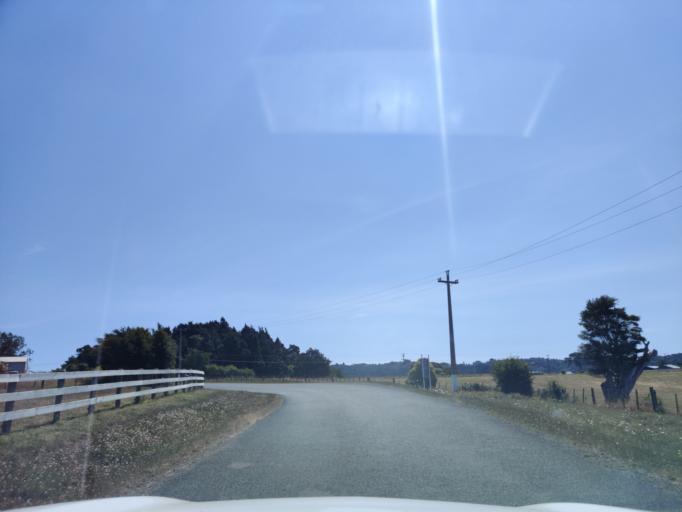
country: NZ
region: Auckland
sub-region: Auckland
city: Red Hill
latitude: -37.0688
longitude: 175.0721
